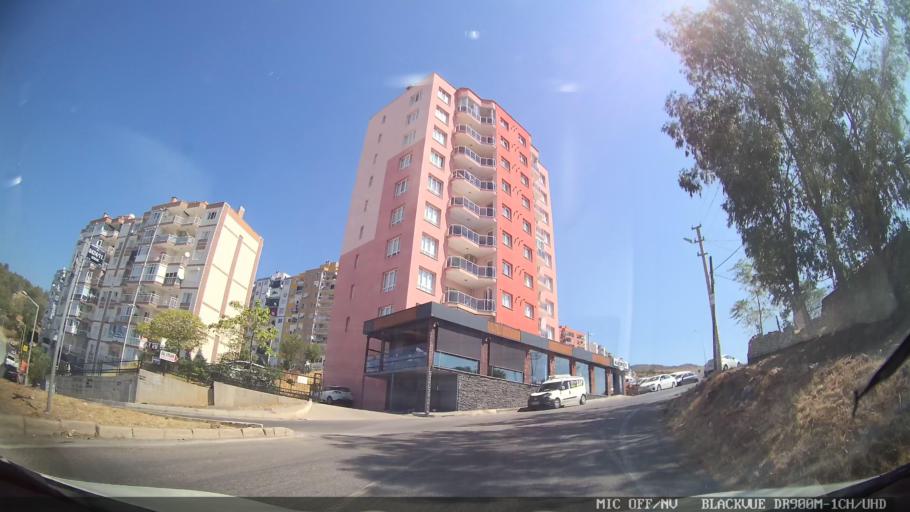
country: TR
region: Izmir
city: Karsiyaka
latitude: 38.5038
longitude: 27.0787
